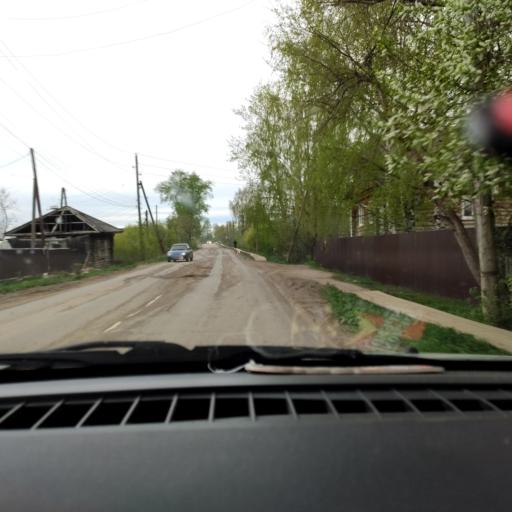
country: RU
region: Perm
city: Kudymkar
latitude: 59.0076
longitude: 54.6518
